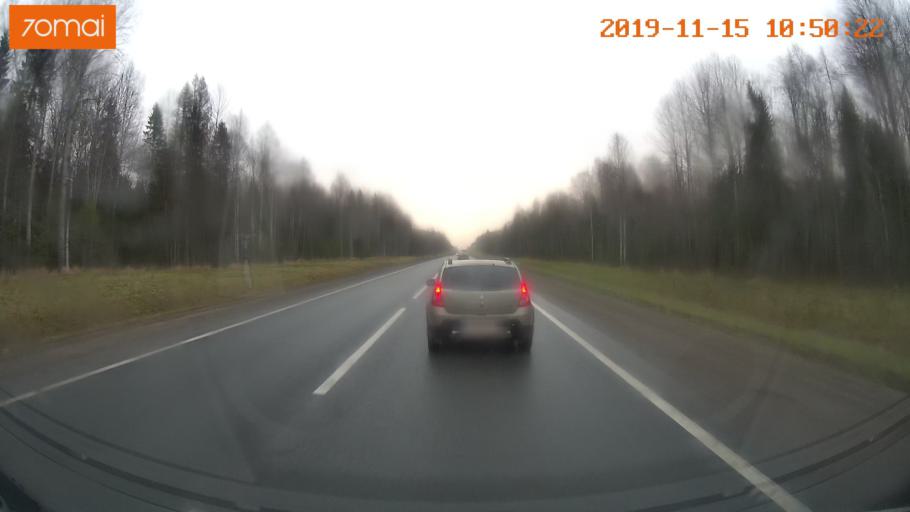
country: RU
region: Vologda
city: Chebsara
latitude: 59.1856
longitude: 38.6801
